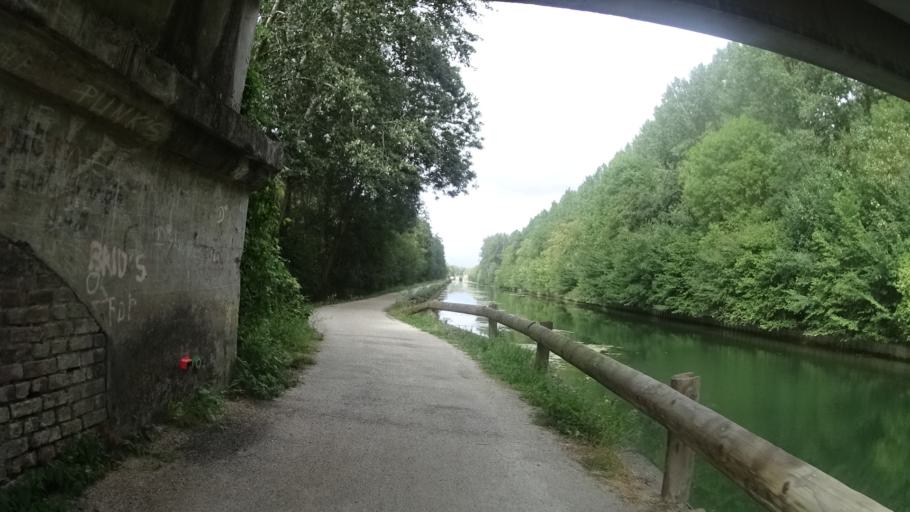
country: FR
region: Picardie
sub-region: Departement de l'Aisne
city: Itancourt
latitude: 49.7629
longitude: 3.3848
